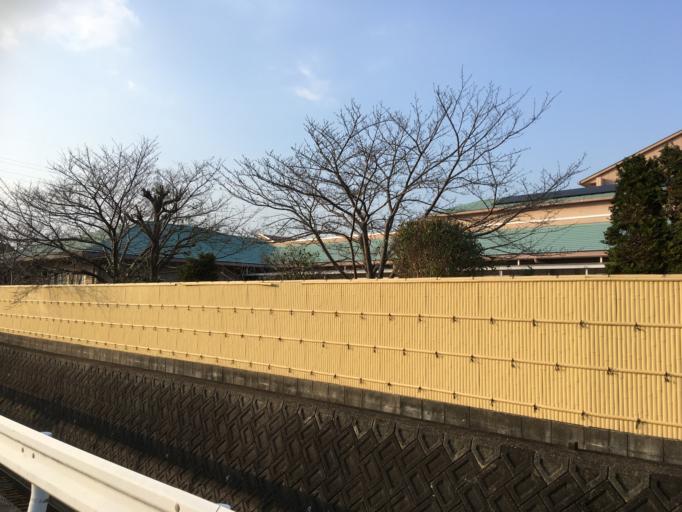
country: JP
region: Nara
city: Tawaramoto
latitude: 34.6015
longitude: 135.7866
